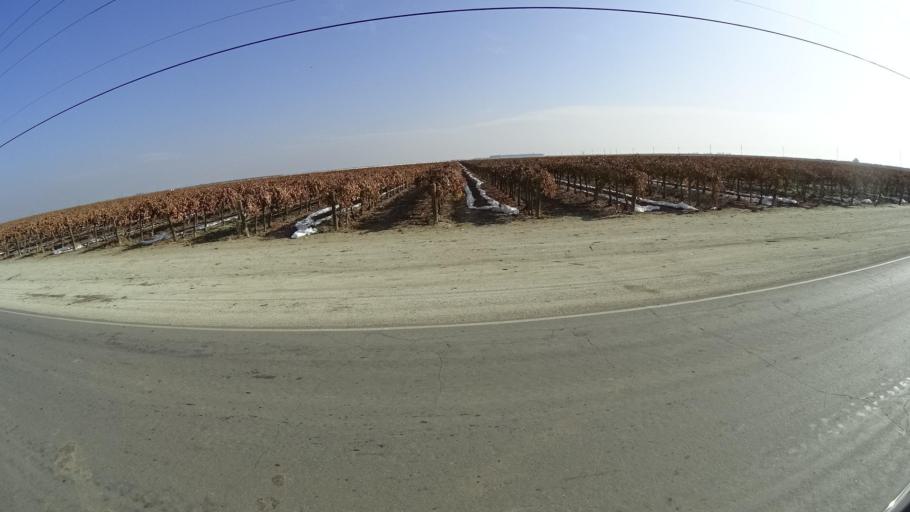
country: US
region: California
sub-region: Kern County
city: McFarland
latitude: 35.7063
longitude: -119.2230
